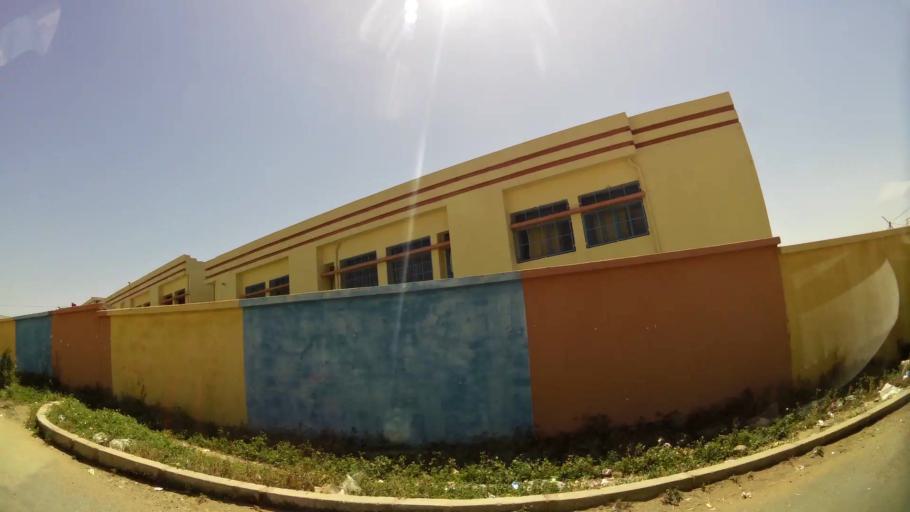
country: MA
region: Rabat-Sale-Zemmour-Zaer
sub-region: Khemisset
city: Khemisset
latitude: 33.8099
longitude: -6.0695
